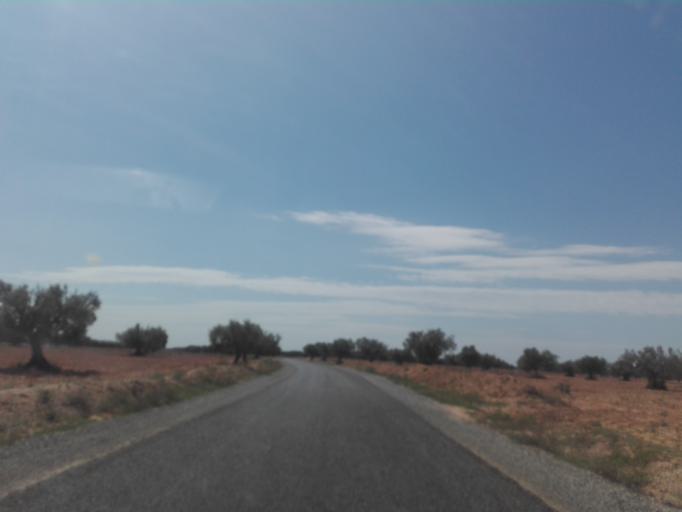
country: TN
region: Safaqis
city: Sfax
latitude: 34.6809
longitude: 10.5689
